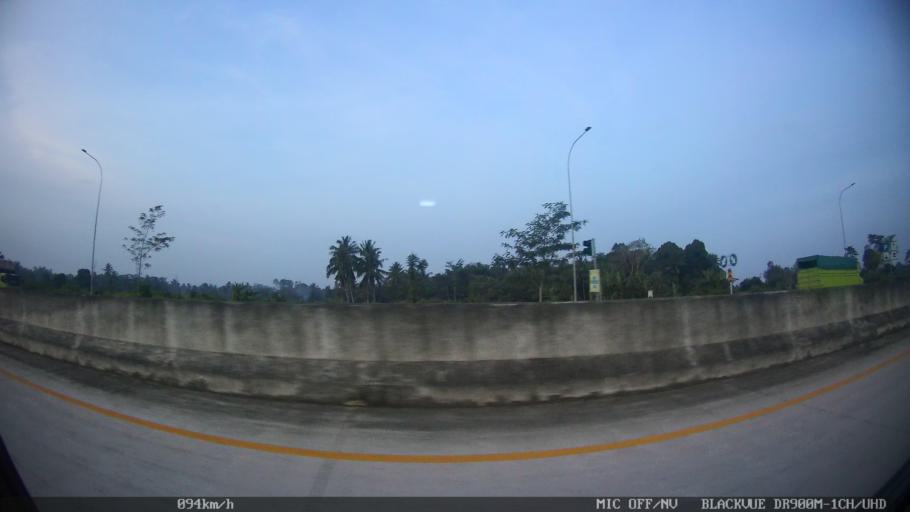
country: ID
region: Lampung
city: Pasuruan
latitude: -5.7239
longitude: 105.6668
